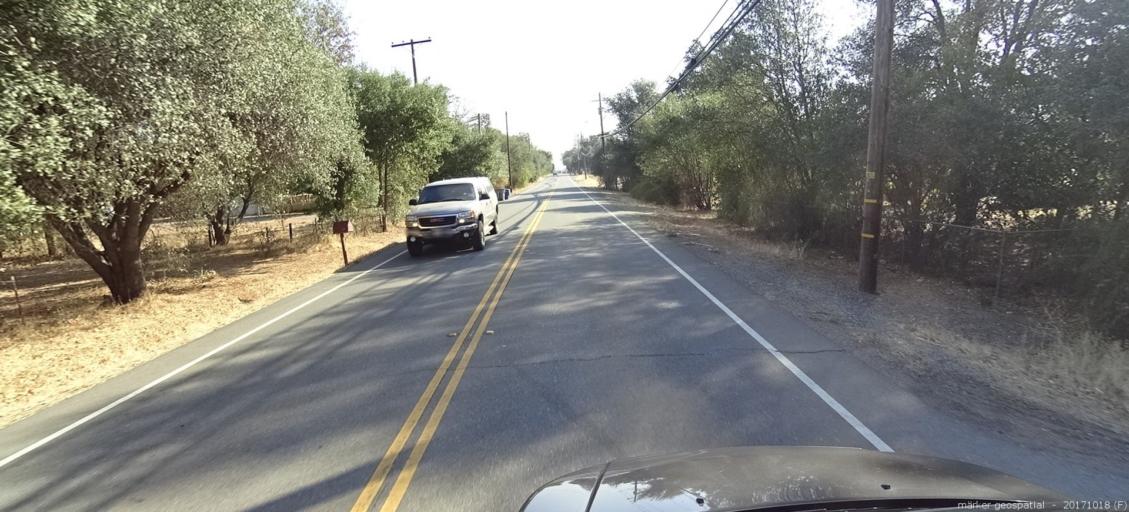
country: US
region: California
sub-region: Shasta County
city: Palo Cedro
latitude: 40.5347
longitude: -122.3099
